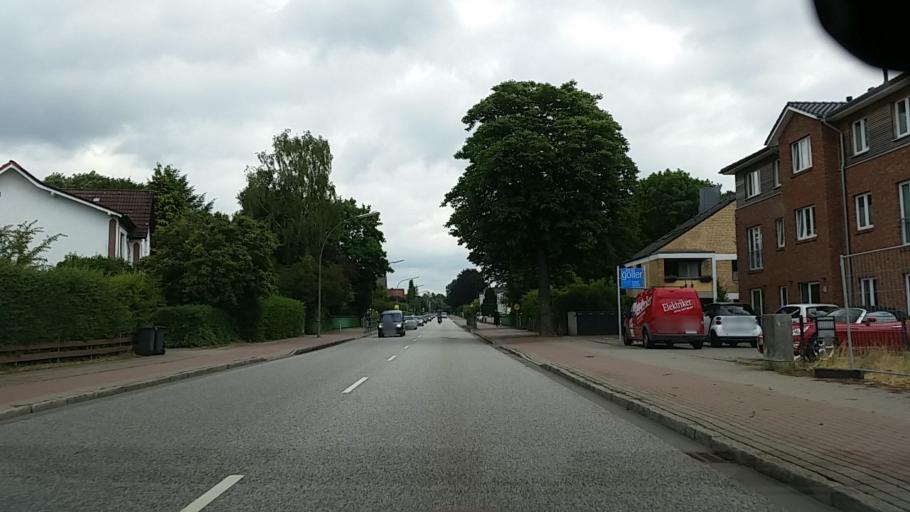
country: DE
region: Schleswig-Holstein
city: Norderstedt
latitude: 53.6778
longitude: 9.9911
